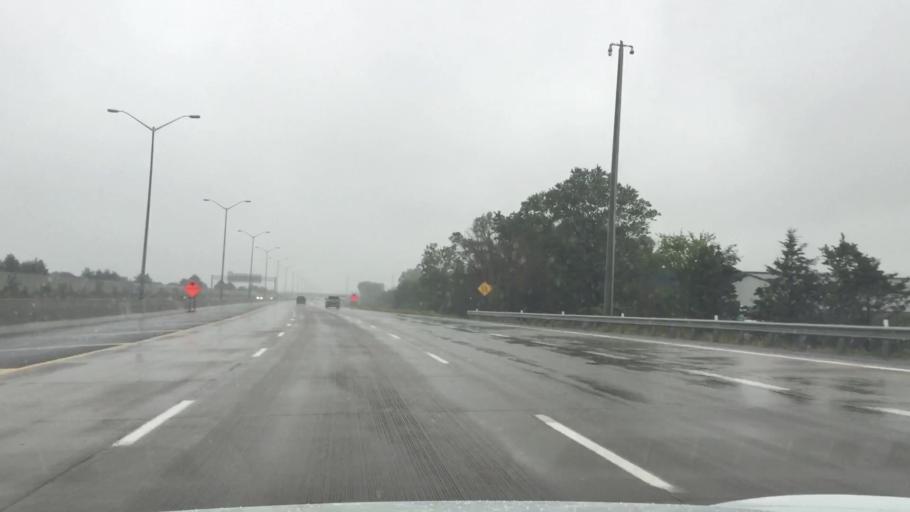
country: CA
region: Ontario
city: Windsor
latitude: 42.2350
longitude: -82.9831
